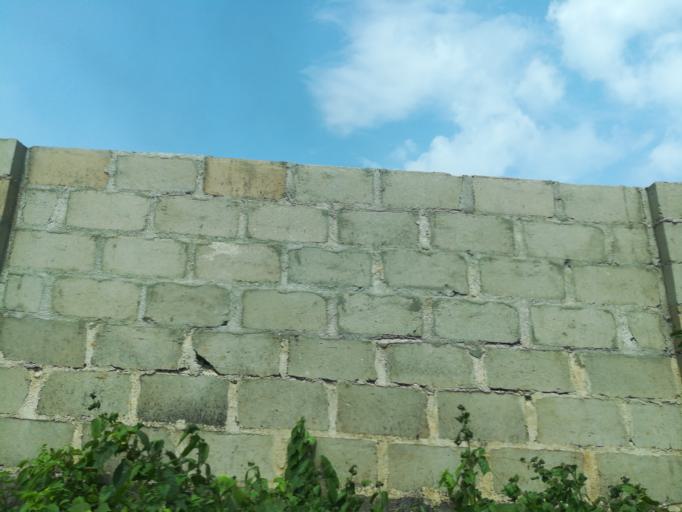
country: NG
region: Lagos
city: Ikorodu
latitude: 6.6021
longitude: 3.6292
